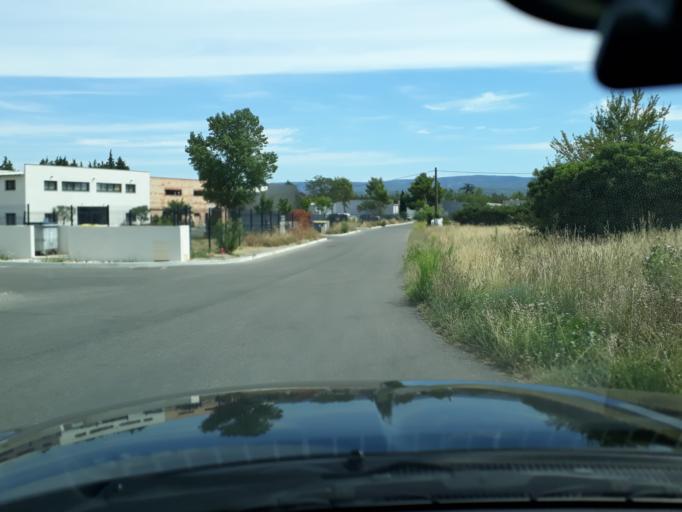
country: FR
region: Provence-Alpes-Cote d'Azur
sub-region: Departement du Vaucluse
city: Carpentras
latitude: 44.0386
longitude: 5.0464
